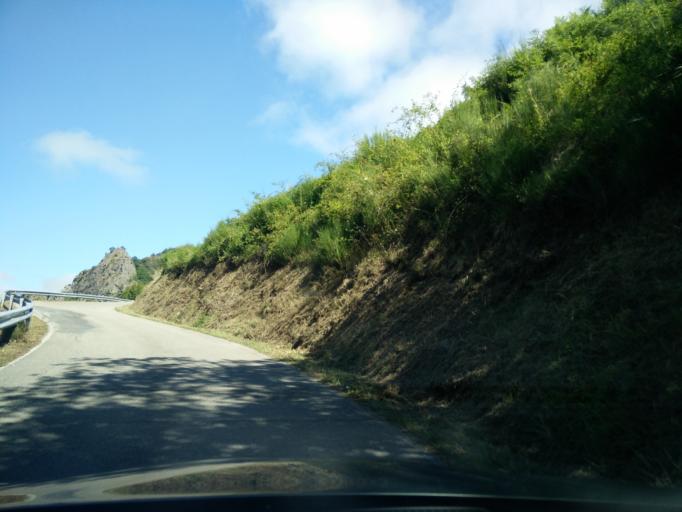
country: ES
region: Asturias
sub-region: Province of Asturias
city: Pola de Somiedo
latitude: 43.0855
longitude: -6.2368
